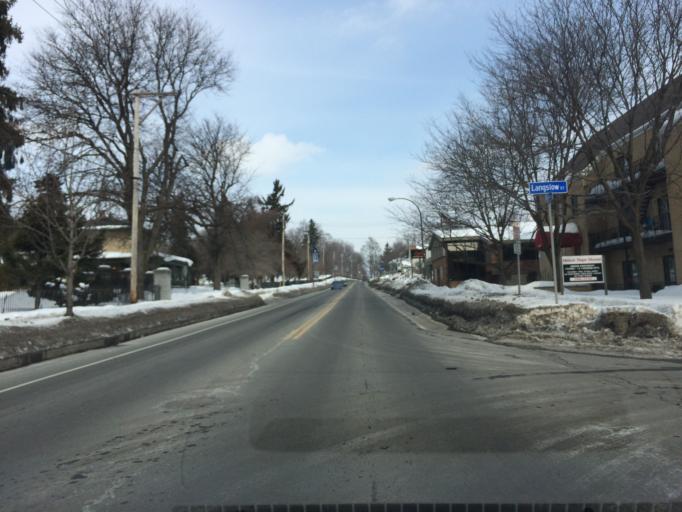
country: US
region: New York
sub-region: Monroe County
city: Rochester
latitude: 43.1271
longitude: -77.6162
